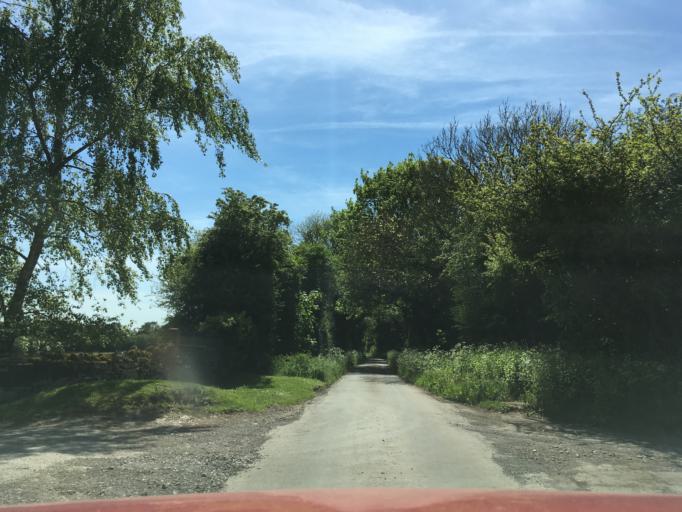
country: GB
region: England
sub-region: Gloucestershire
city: Brimscombe
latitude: 51.7371
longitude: -2.1833
